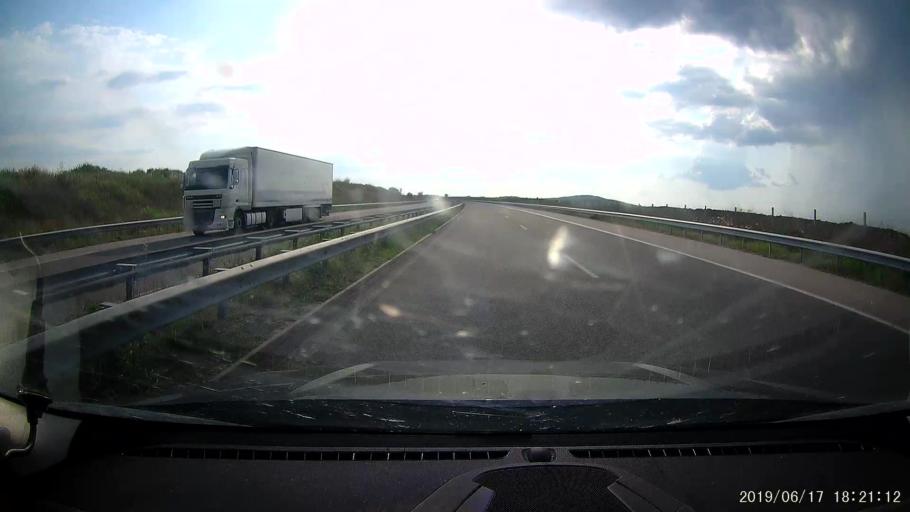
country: BG
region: Khaskovo
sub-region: Obshtina Simeonovgrad
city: Simeonovgrad
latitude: 41.9673
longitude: 25.7906
